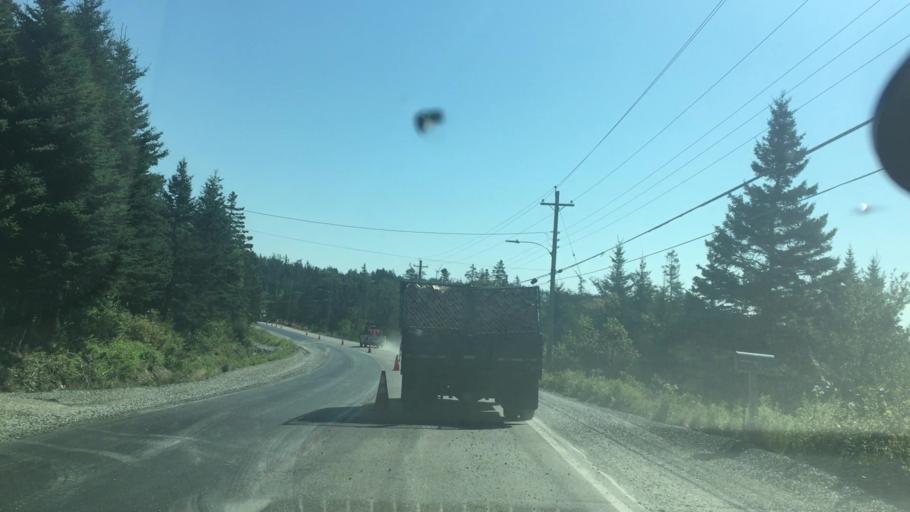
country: CA
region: Nova Scotia
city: New Glasgow
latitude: 44.9074
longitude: -62.4966
